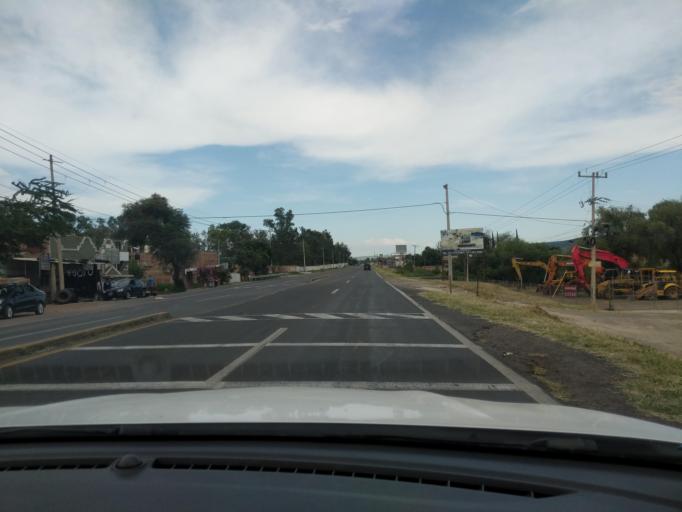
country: MX
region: Jalisco
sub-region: El Salto
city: Galaxia Bonito Jalisco
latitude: 20.5105
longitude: -103.1969
